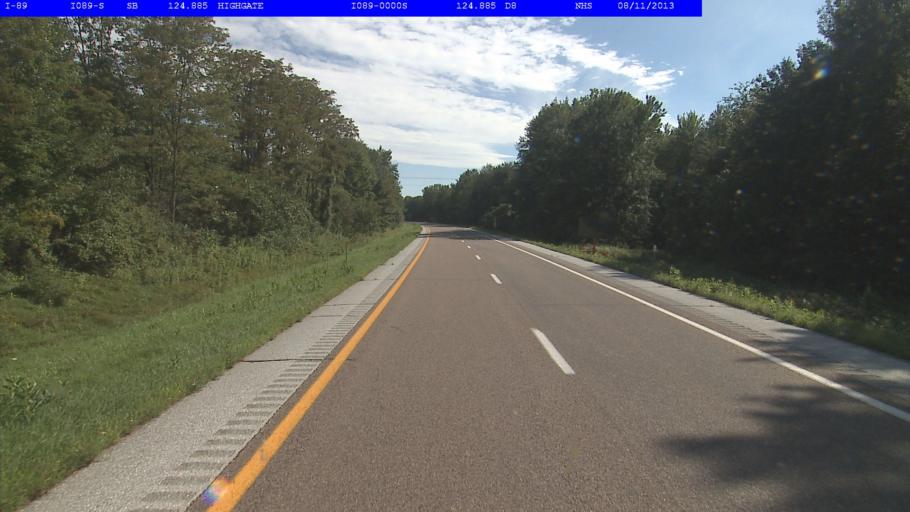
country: US
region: Vermont
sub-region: Franklin County
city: Swanton
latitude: 44.9433
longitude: -73.1150
